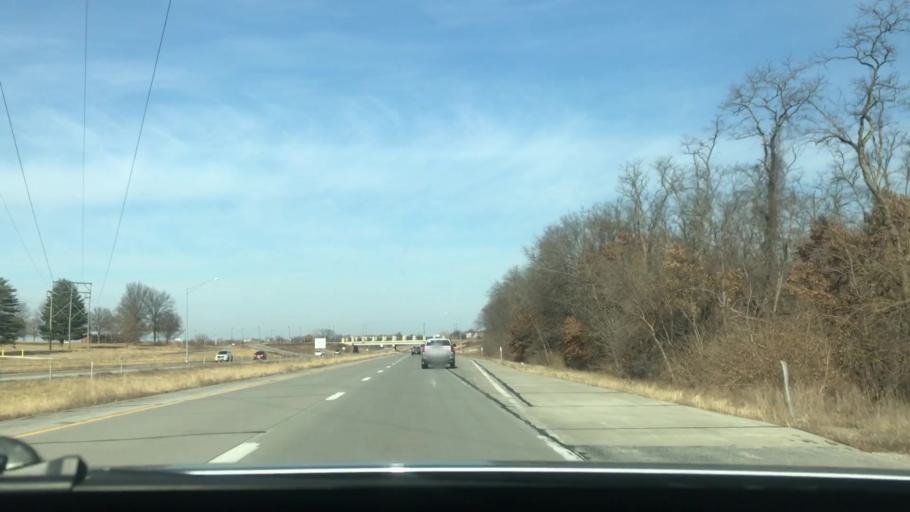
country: US
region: Missouri
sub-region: Clay County
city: Gladstone
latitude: 39.2843
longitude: -94.5850
